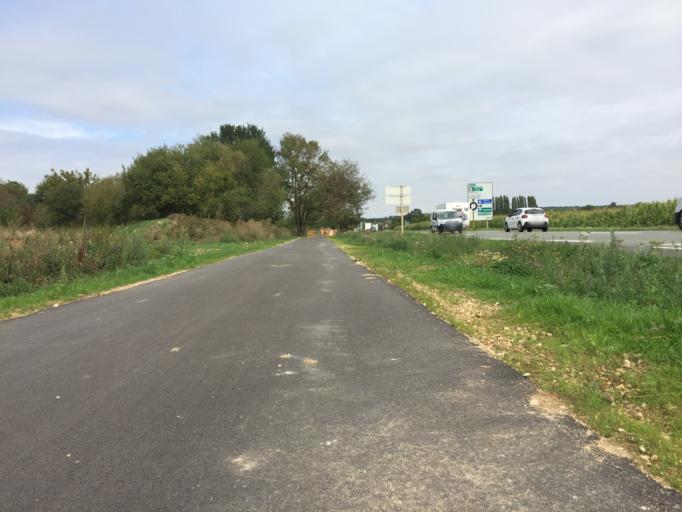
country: FR
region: Picardie
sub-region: Departement de l'Oise
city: Auneuil
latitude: 49.3873
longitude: 2.0041
